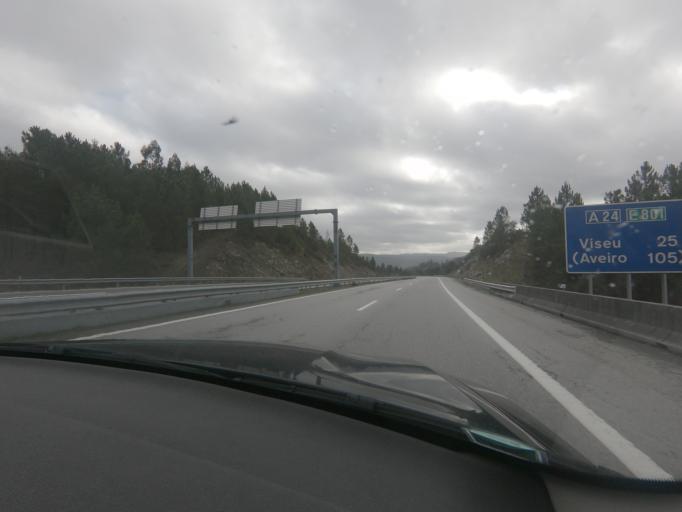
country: PT
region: Viseu
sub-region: Castro Daire
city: Castro Daire
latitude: 40.8136
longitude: -7.9387
